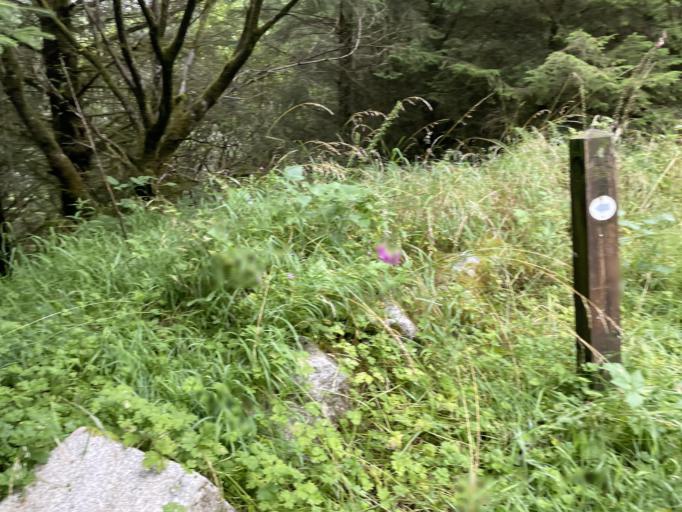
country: GB
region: Scotland
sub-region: South Ayrshire
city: Maybole
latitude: 55.2041
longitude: -4.6735
